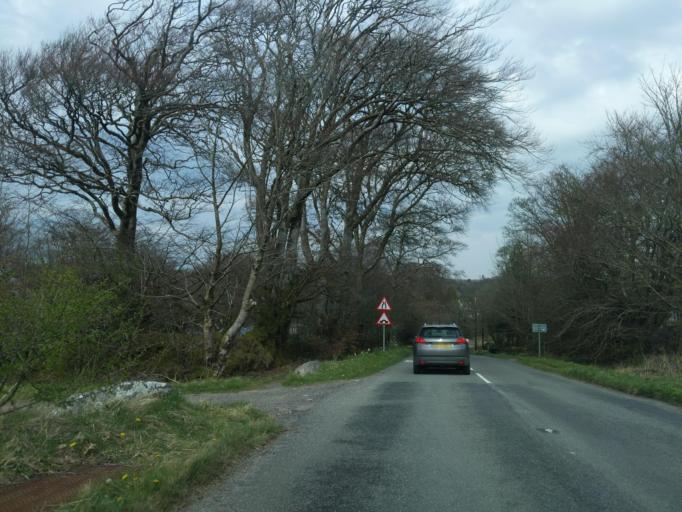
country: GB
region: England
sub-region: Devon
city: Okehampton
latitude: 50.5929
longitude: -3.9139
